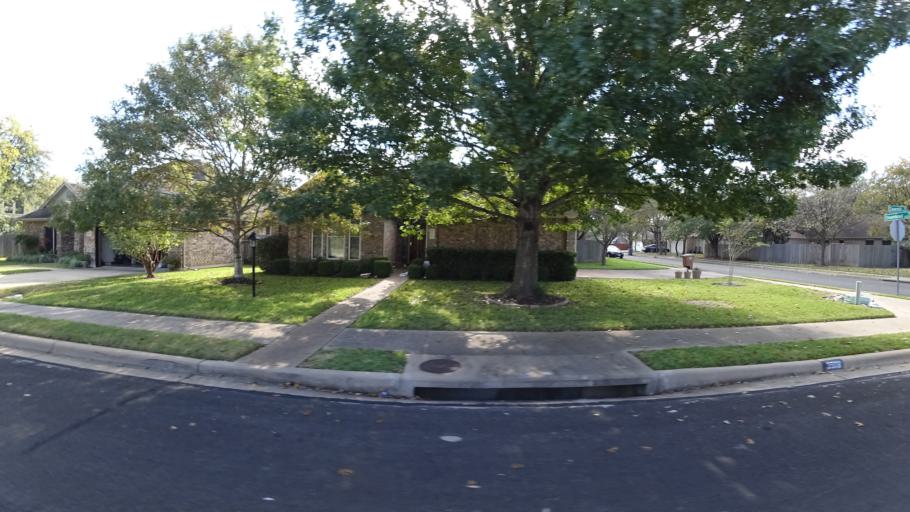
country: US
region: Texas
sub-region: Travis County
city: Shady Hollow
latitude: 30.1818
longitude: -97.8527
